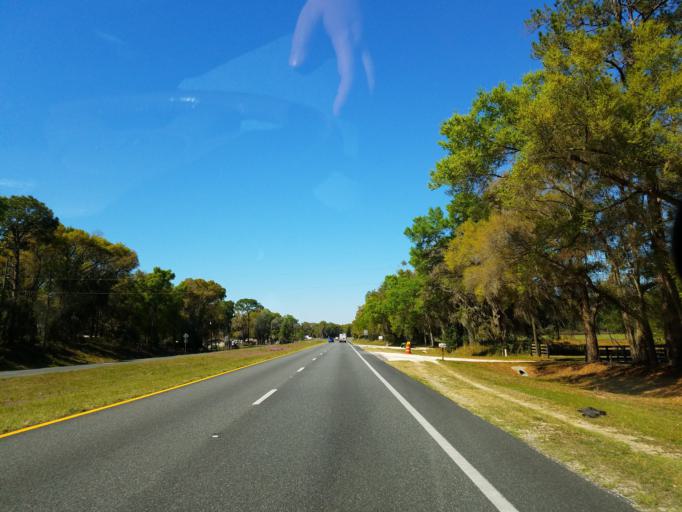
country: US
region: Florida
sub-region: Marion County
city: Belleview
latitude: 29.0158
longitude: -82.0442
